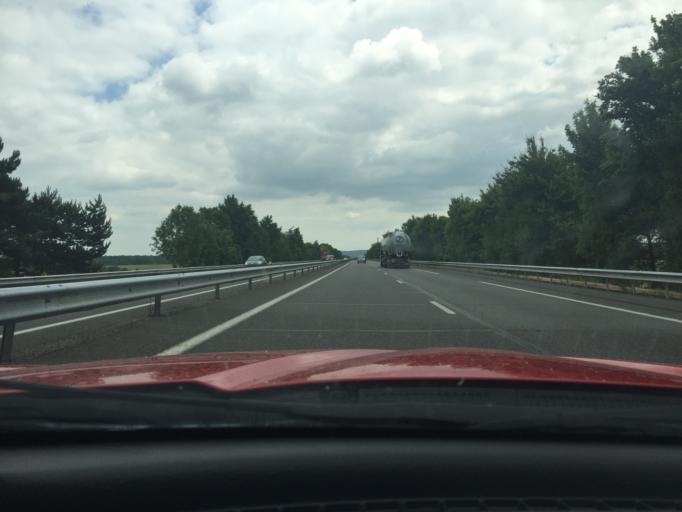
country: FR
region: Picardie
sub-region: Departement de l'Aisne
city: Athies-sous-Laon
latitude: 49.5840
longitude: 3.6906
